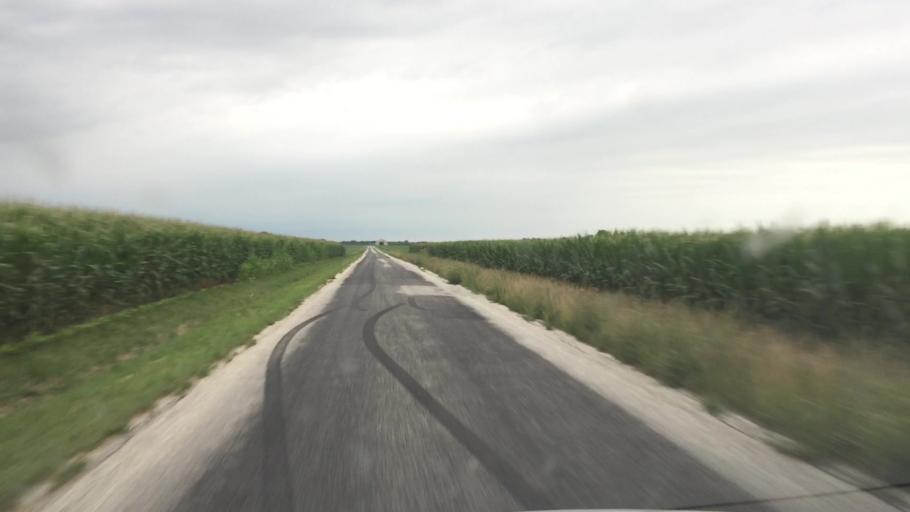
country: US
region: Illinois
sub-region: Adams County
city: Camp Point
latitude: 40.2212
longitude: -90.9691
